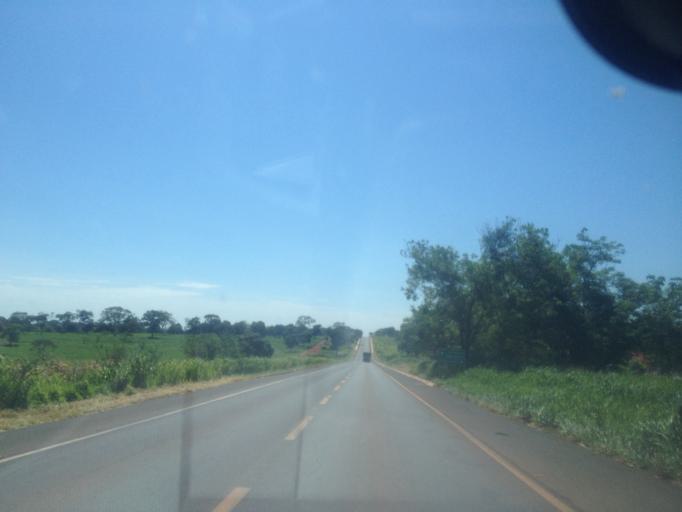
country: BR
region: Minas Gerais
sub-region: Santa Vitoria
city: Santa Vitoria
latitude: -18.9322
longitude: -49.8358
